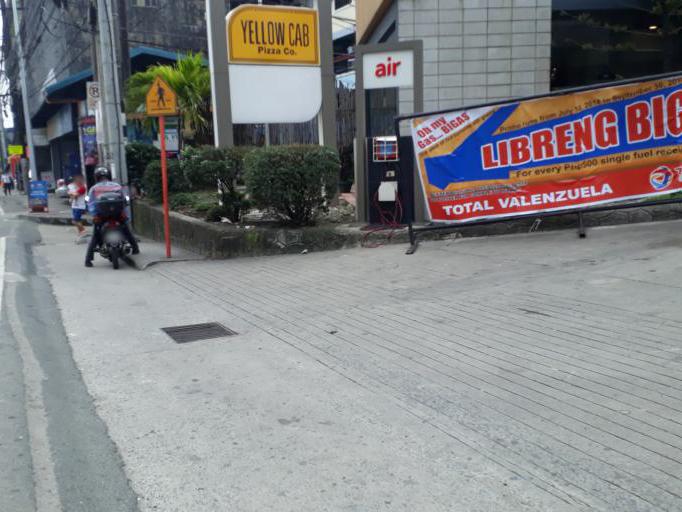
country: PH
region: Calabarzon
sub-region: Province of Rizal
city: Valenzuela
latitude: 14.6847
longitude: 120.9769
